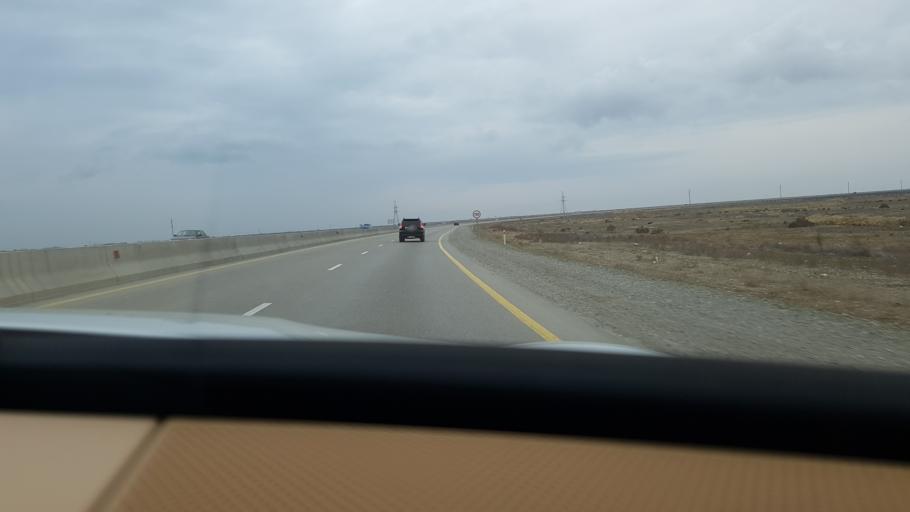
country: AZ
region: Haciqabul
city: Haciqabul
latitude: 40.0070
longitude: 48.9039
